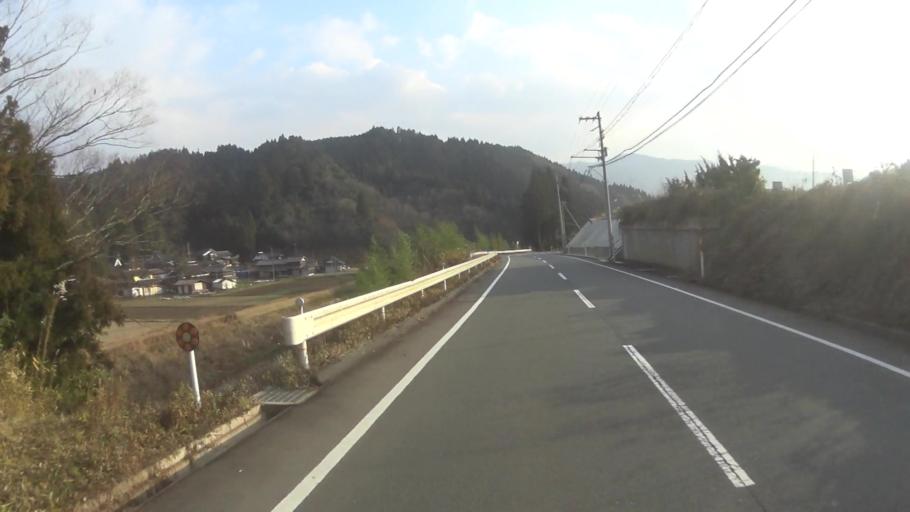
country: JP
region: Kyoto
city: Maizuru
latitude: 35.3810
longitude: 135.4190
